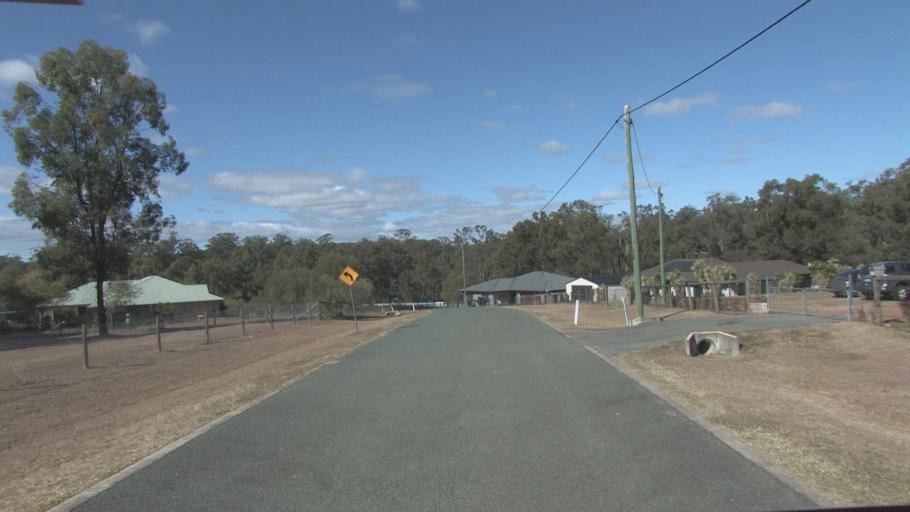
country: AU
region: Queensland
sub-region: Logan
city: Cedar Vale
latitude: -27.8820
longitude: 153.0053
